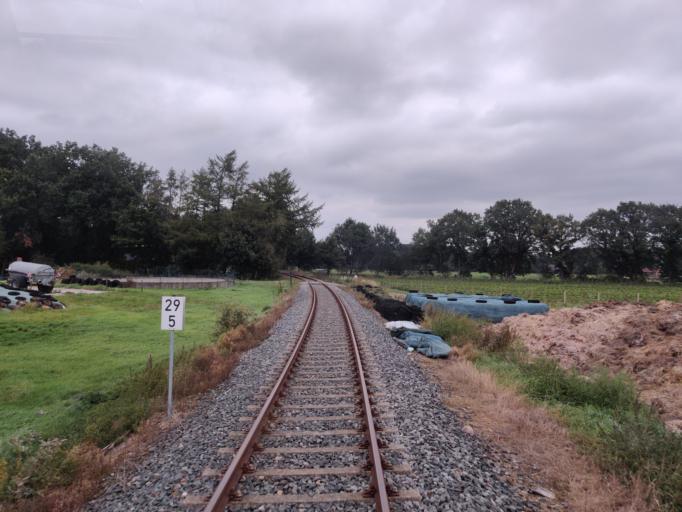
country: DE
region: Lower Saxony
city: Vollersode
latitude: 53.2920
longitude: 8.9712
